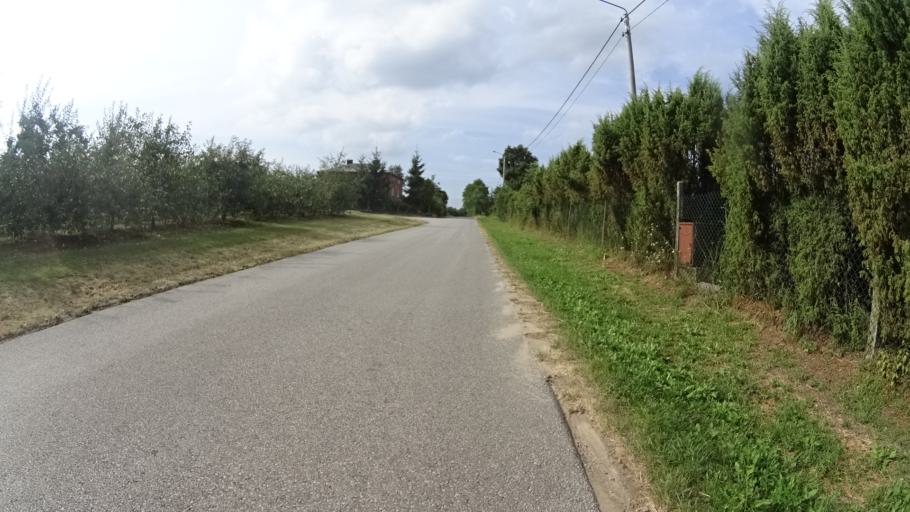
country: PL
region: Masovian Voivodeship
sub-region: Powiat grojecki
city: Goszczyn
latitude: 51.7049
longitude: 20.8443
